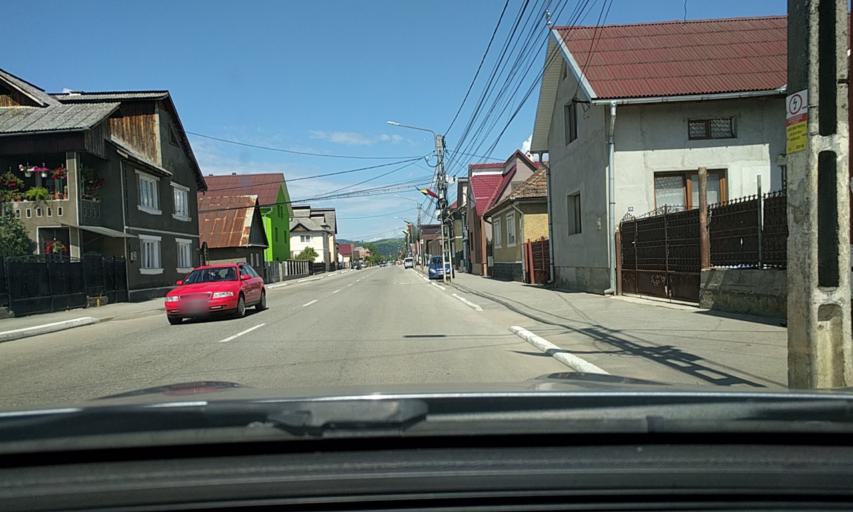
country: RO
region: Bistrita-Nasaud
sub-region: Oras Nasaud
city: Nasaud
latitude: 47.2899
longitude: 24.3913
